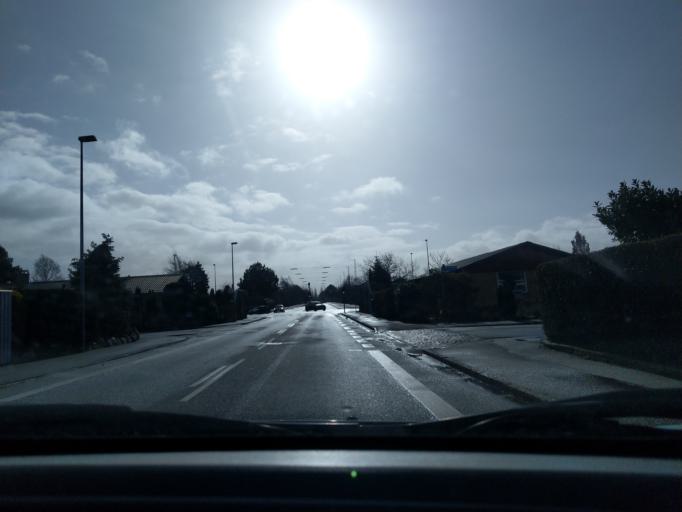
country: DK
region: Zealand
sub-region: Naestved Kommune
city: Naestved
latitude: 55.2172
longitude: 11.7689
